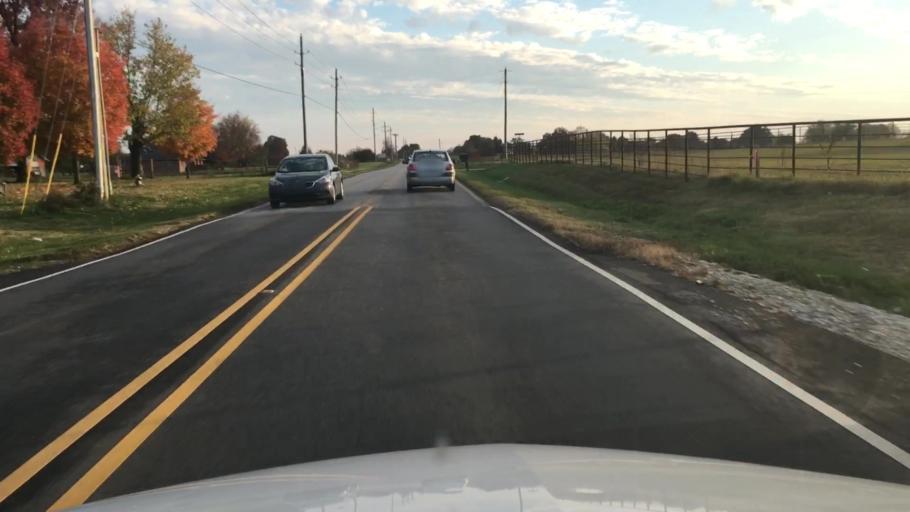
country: US
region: Arkansas
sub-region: Washington County
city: Elm Springs
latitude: 36.2237
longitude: -94.2304
